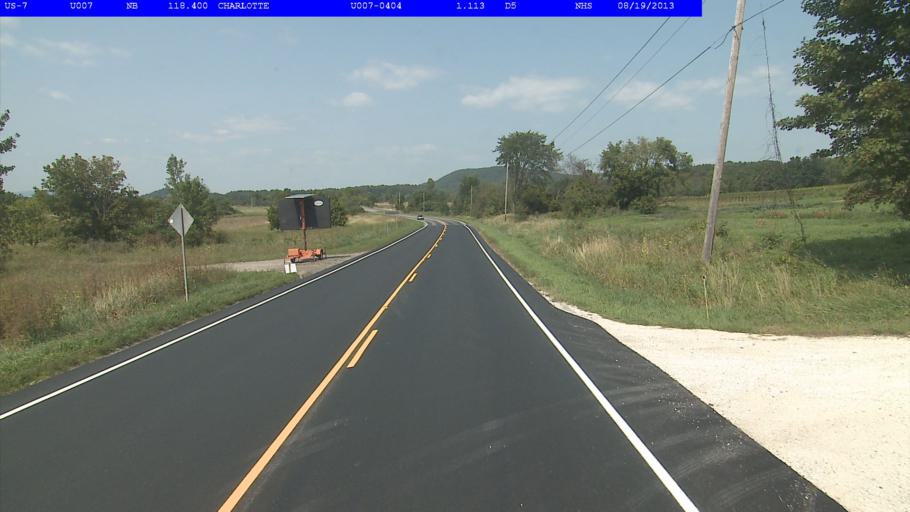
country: US
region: Vermont
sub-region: Addison County
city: Vergennes
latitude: 44.2782
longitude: -73.2351
